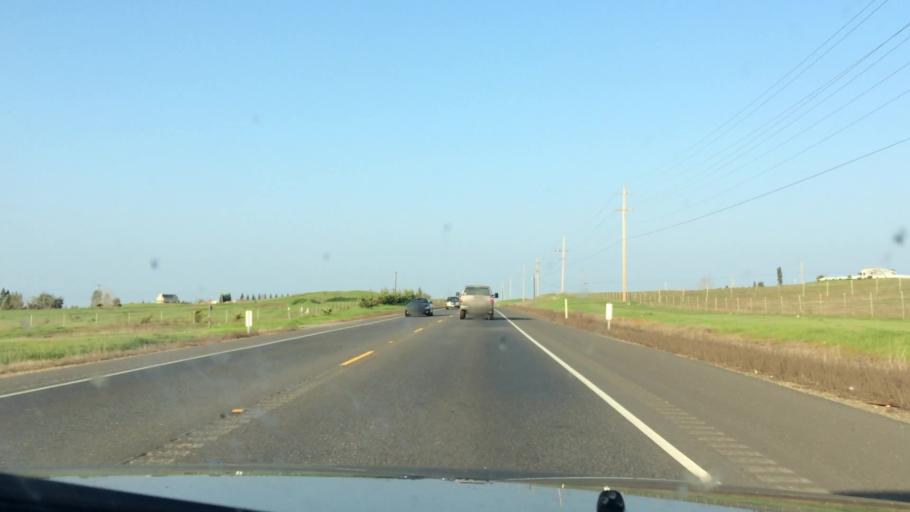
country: US
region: California
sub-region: Sacramento County
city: Rancho Murieta
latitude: 38.4948
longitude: -121.1335
